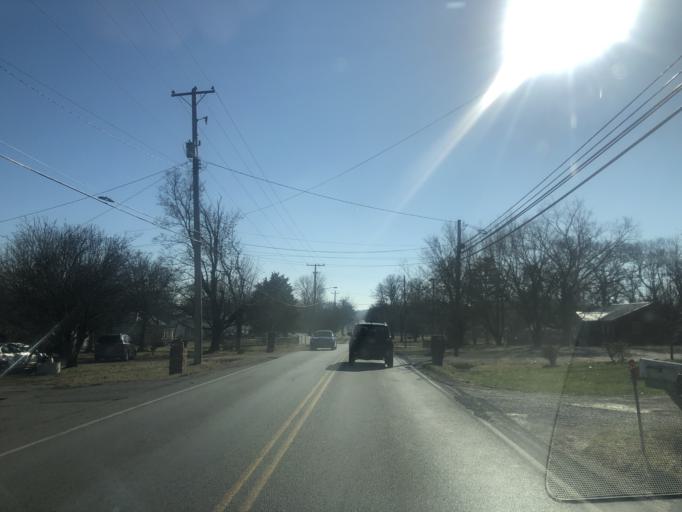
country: US
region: Tennessee
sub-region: Rutherford County
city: La Vergne
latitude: 36.0106
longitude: -86.5706
